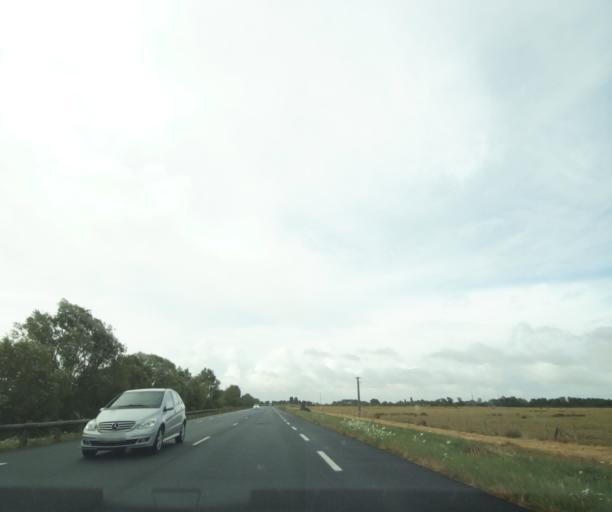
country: FR
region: Pays de la Loire
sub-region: Departement de la Vendee
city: Champagne-les-Marais
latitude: 46.3843
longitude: -1.0925
